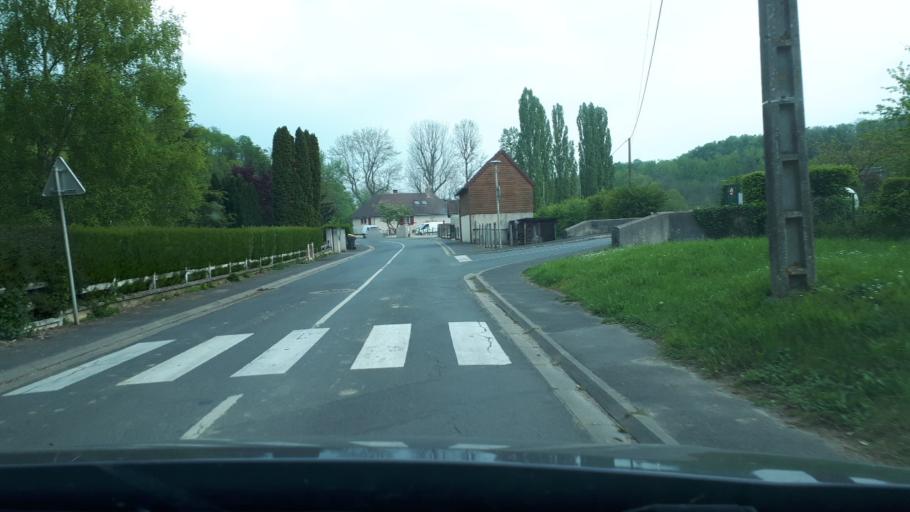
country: FR
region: Centre
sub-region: Departement du Loir-et-Cher
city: Lunay
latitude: 47.8216
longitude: 0.9477
